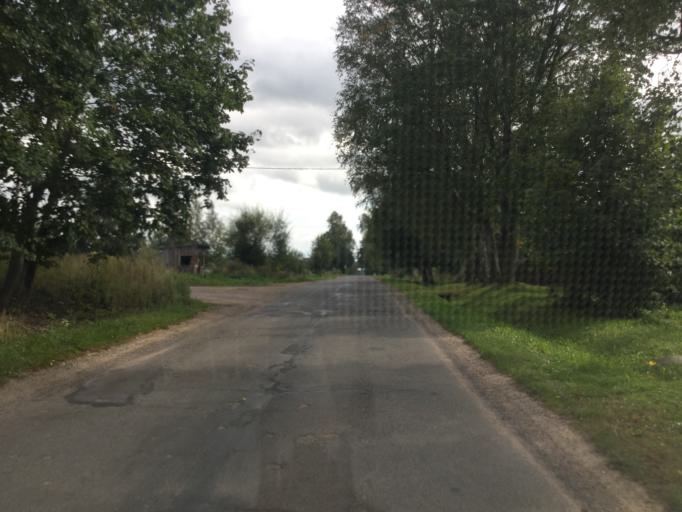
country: BY
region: Vitebsk
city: Vitebsk
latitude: 55.1465
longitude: 30.2820
